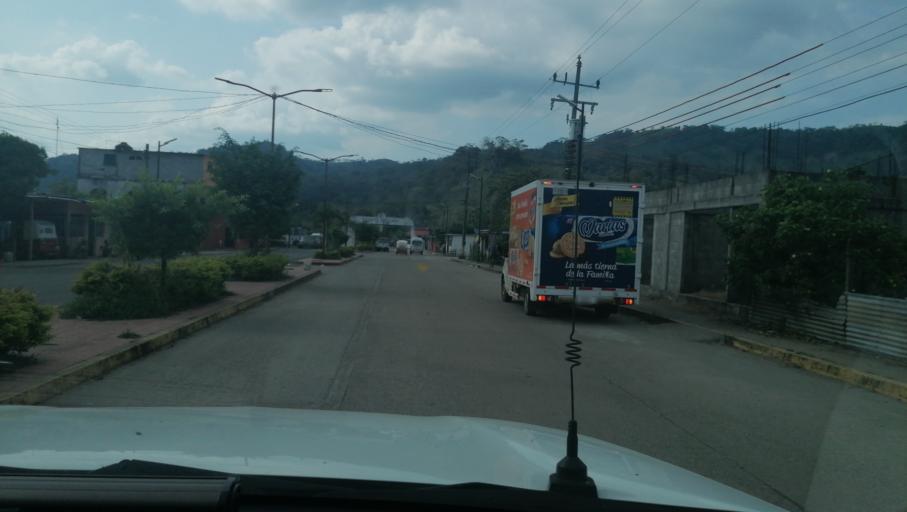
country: MX
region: Chiapas
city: Ostuacan
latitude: 17.4136
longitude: -93.3364
